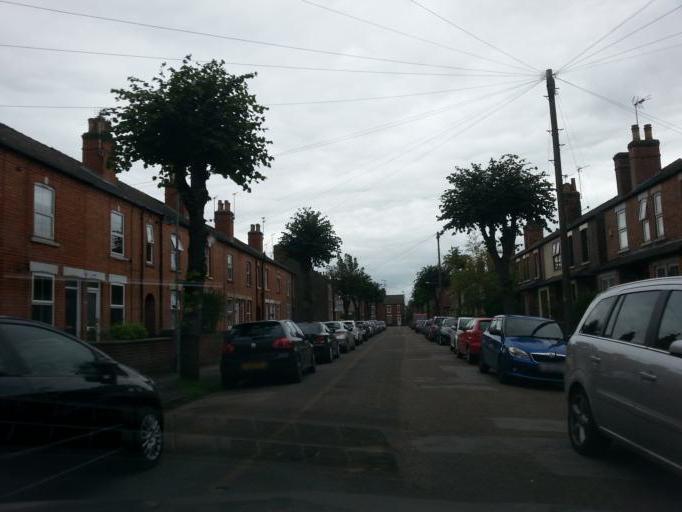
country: GB
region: England
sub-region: Nottinghamshire
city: Newark on Trent
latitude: 53.0715
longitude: -0.7980
